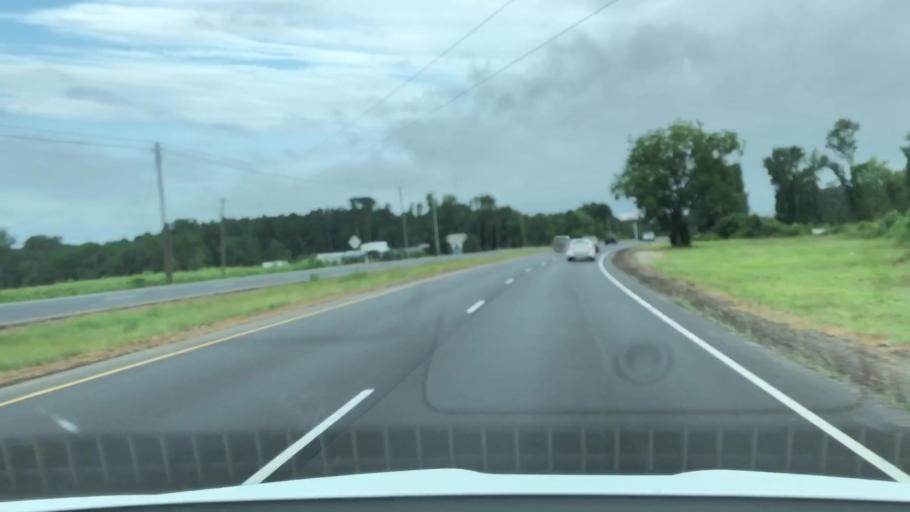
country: US
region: North Carolina
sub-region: Lenoir County
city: Kinston
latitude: 35.2464
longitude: -77.5908
